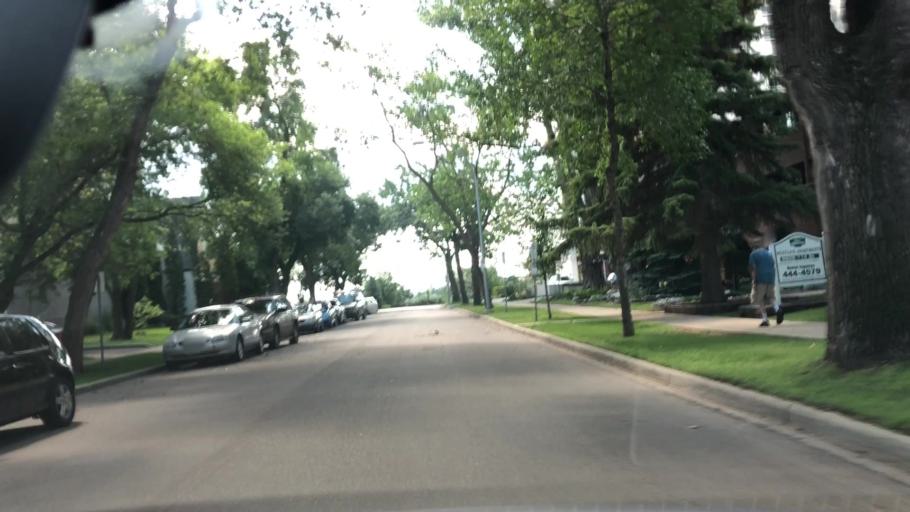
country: CA
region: Alberta
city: Edmonton
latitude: 53.5384
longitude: -113.5176
